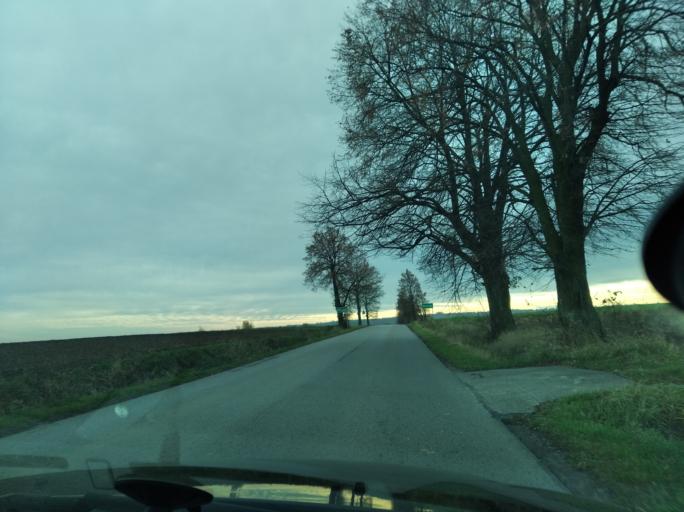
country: PL
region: Subcarpathian Voivodeship
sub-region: Powiat lancucki
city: Wysoka
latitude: 50.0226
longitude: 22.2596
